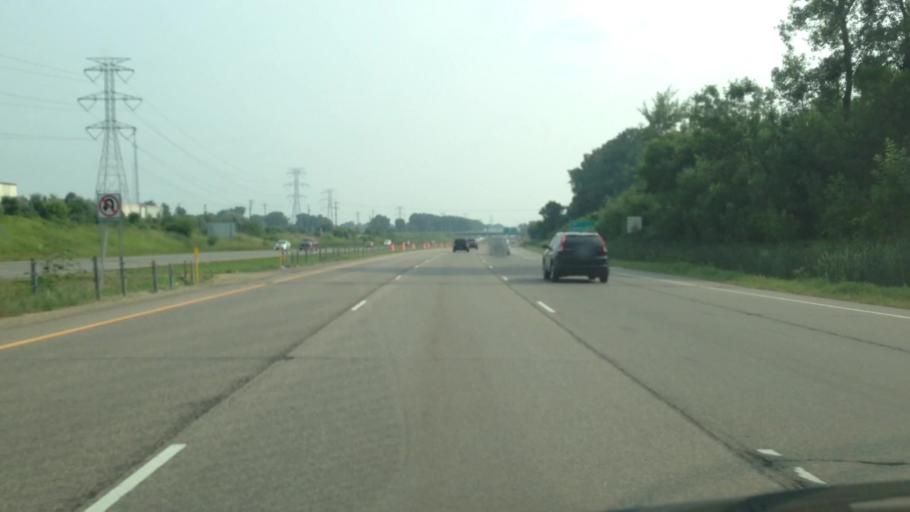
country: US
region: Minnesota
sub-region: Ramsey County
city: New Brighton
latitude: 45.0747
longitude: -93.1855
